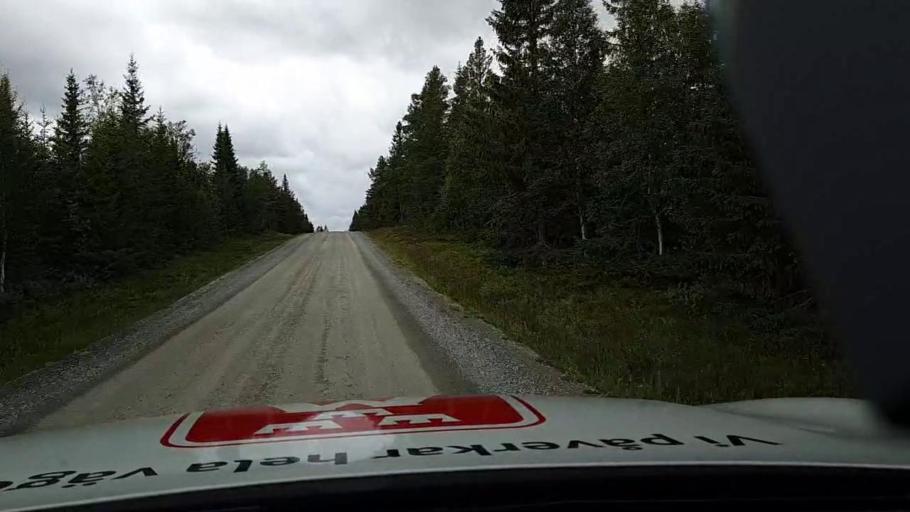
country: SE
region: Jaemtland
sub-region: Bergs Kommun
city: Hoverberg
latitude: 62.8938
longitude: 14.0471
